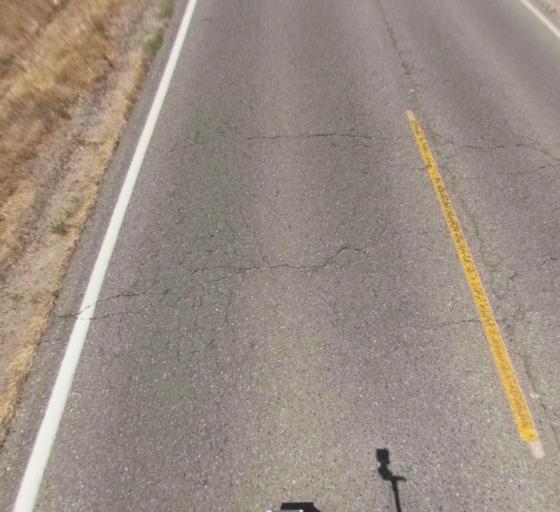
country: US
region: California
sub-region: Madera County
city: Bonadelle Ranchos-Madera Ranchos
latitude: 36.9550
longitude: -119.8939
